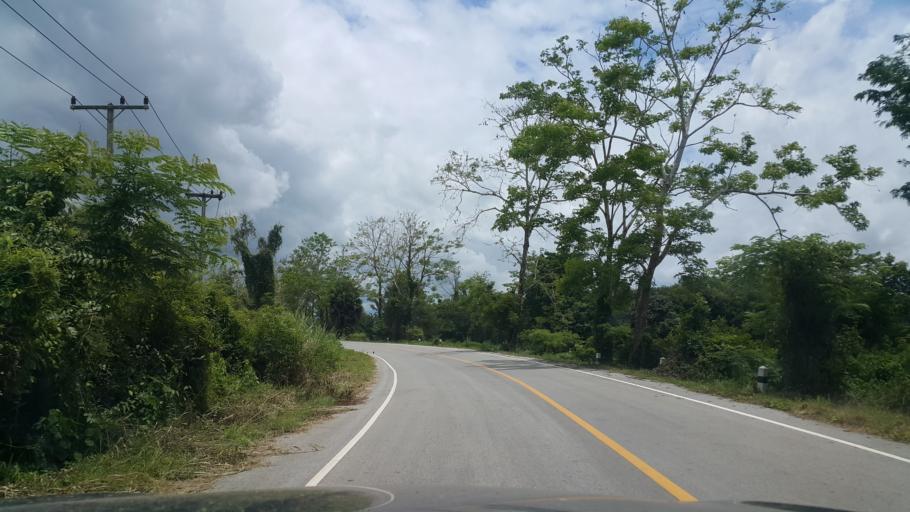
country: TH
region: Sukhothai
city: Kong Krailat
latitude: 16.9353
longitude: 99.9244
